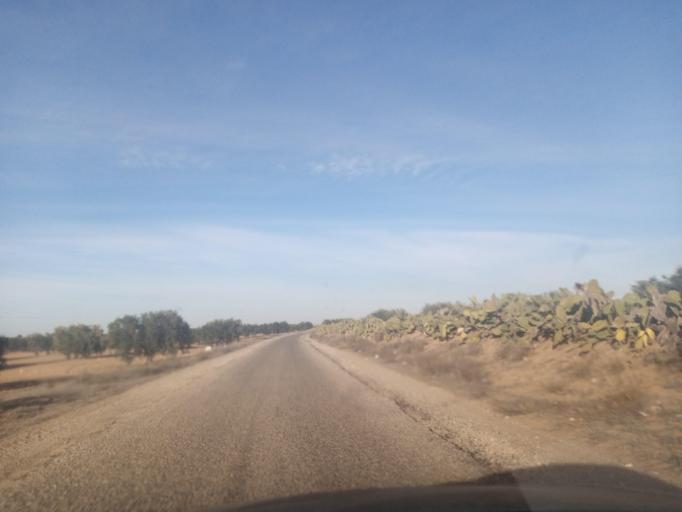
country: TN
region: Safaqis
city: Bi'r `Ali Bin Khalifah
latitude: 34.8745
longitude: 10.1687
